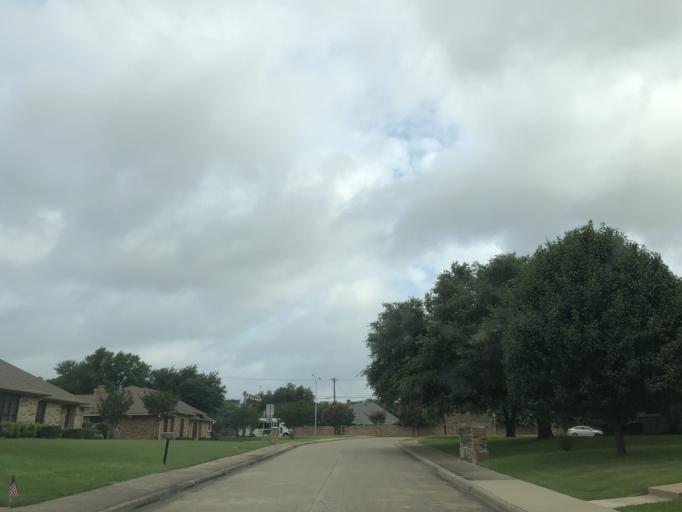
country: US
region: Texas
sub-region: Dallas County
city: Garland
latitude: 32.8365
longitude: -96.6464
